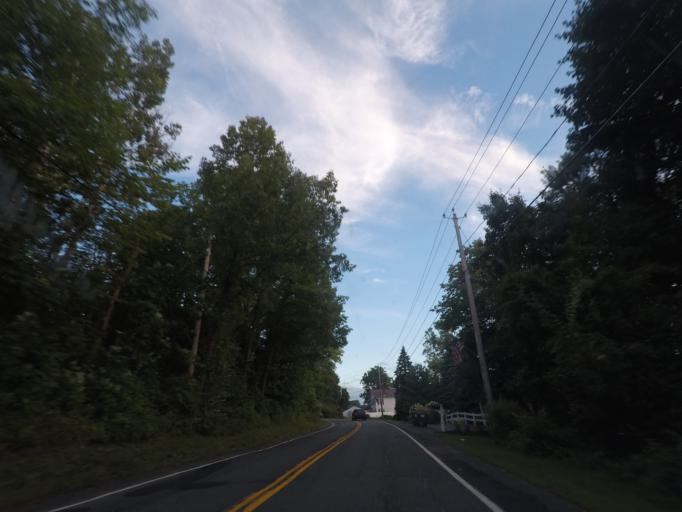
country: US
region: New York
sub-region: Schenectady County
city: Niskayuna
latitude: 42.7783
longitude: -73.7880
